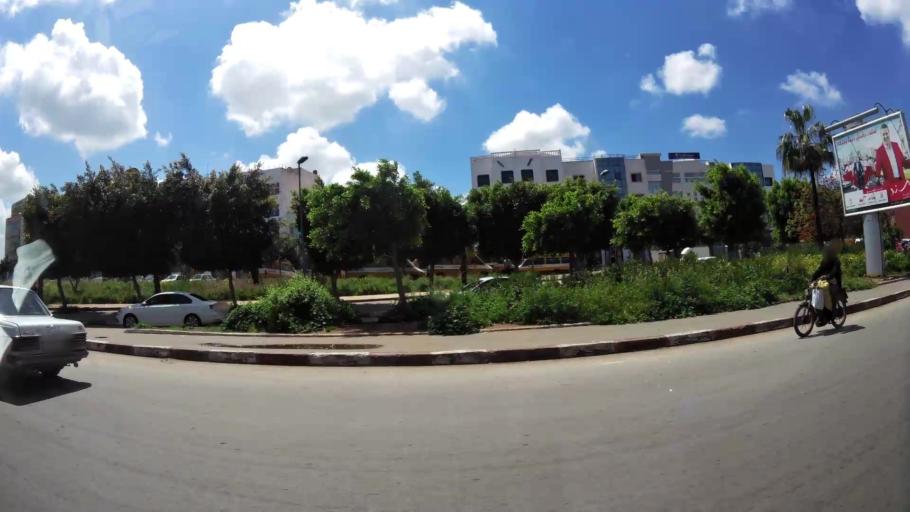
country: MA
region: Grand Casablanca
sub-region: Casablanca
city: Casablanca
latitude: 33.5356
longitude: -7.5751
